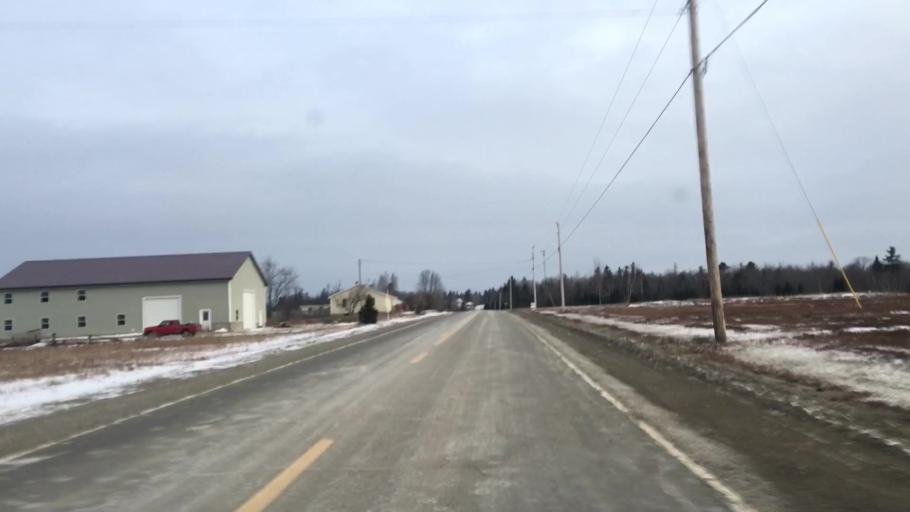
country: US
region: Maine
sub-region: Hancock County
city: Franklin
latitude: 44.7181
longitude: -68.3361
